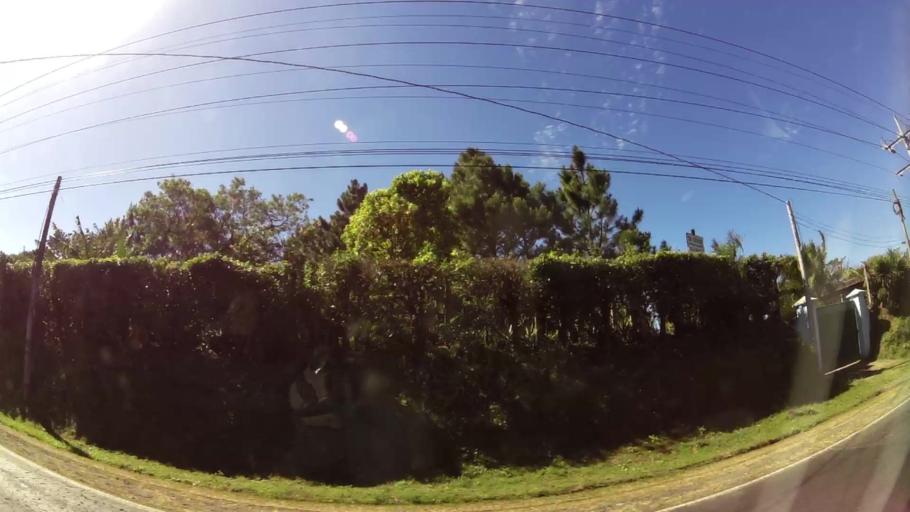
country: SV
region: Ahuachapan
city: Concepcion de Ataco
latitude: 13.8558
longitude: -89.8469
